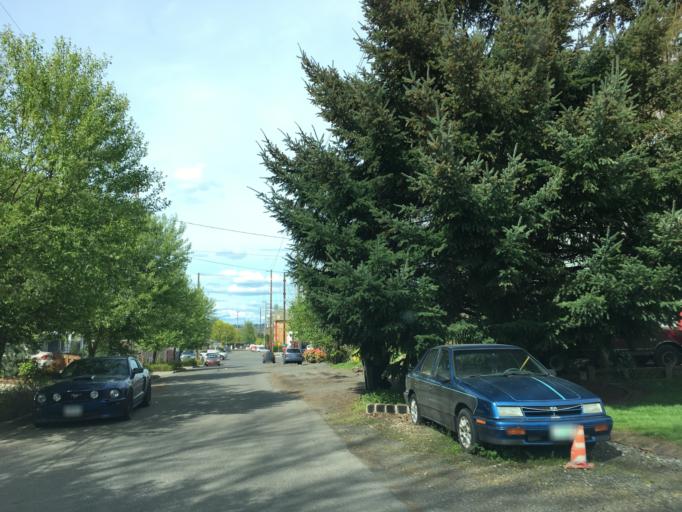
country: US
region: Oregon
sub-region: Multnomah County
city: Lents
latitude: 45.5580
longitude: -122.5588
